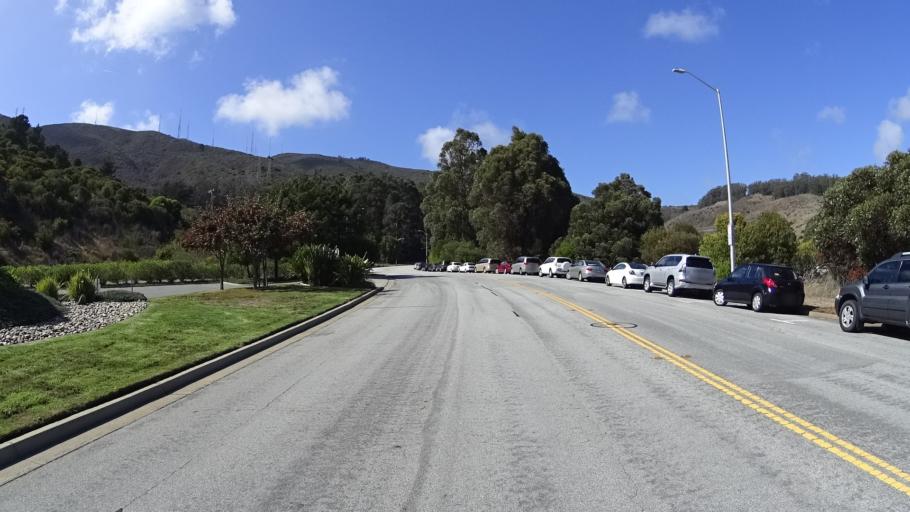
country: US
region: California
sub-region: San Mateo County
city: Brisbane
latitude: 37.6898
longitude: -122.4195
